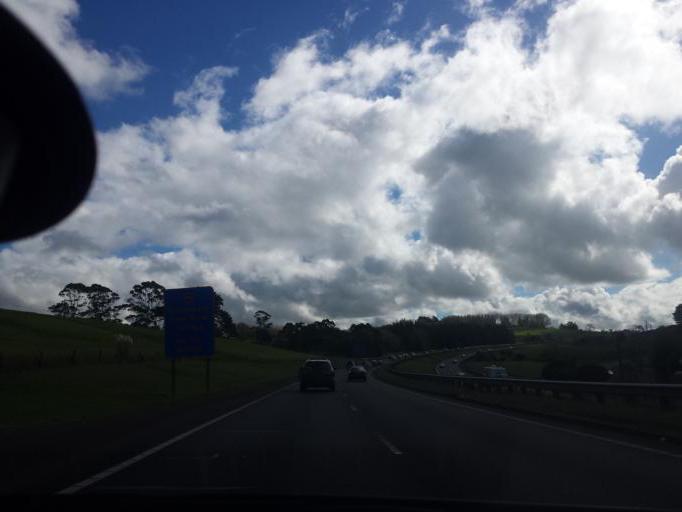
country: NZ
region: Auckland
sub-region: Auckland
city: Rothesay Bay
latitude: -36.6793
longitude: 174.6913
